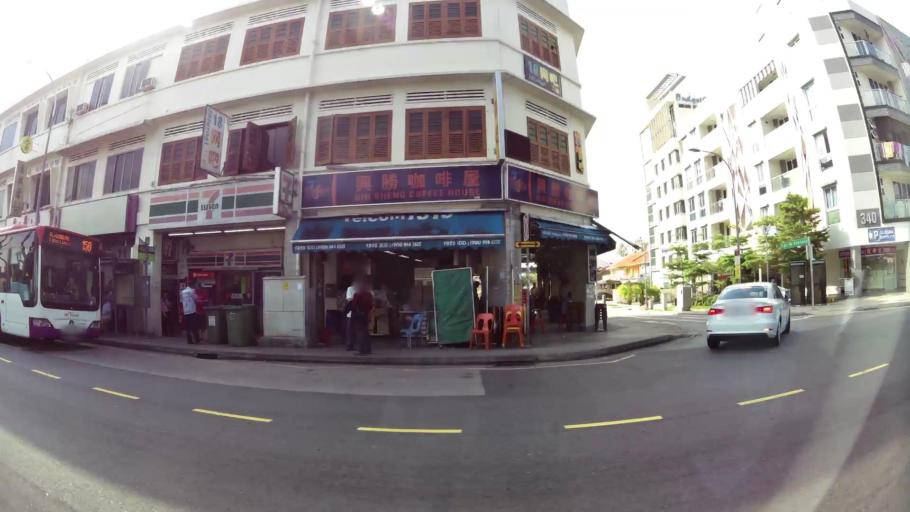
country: SG
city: Singapore
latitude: 1.3127
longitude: 103.8806
